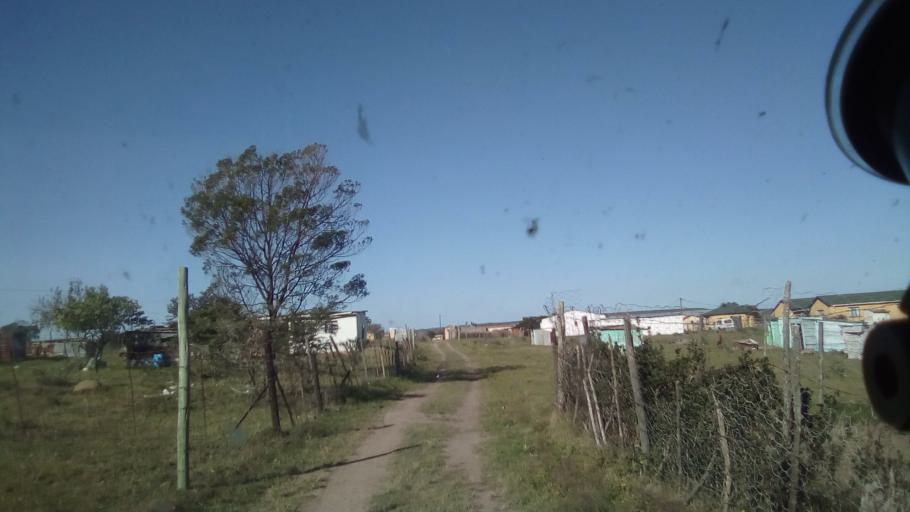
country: ZA
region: Eastern Cape
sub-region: Buffalo City Metropolitan Municipality
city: Bhisho
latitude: -32.8252
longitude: 27.3685
